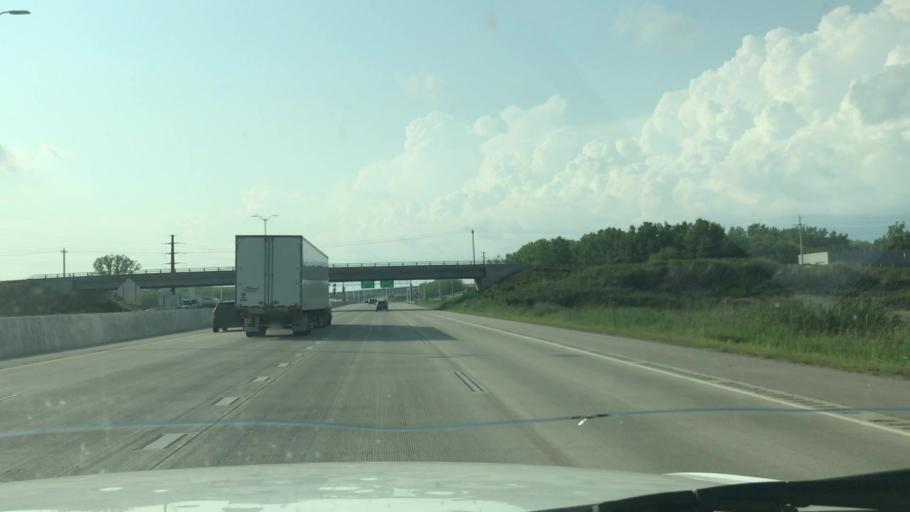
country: US
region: Wisconsin
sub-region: Brown County
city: Green Bay
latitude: 44.5517
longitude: -88.0411
